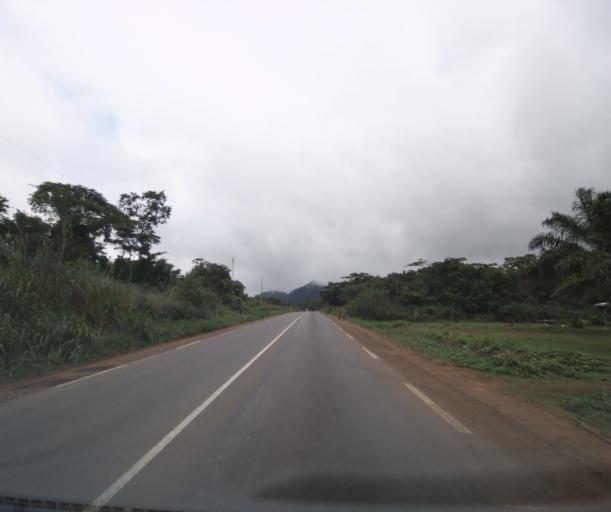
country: CM
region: Centre
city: Mbankomo
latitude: 3.8005
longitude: 11.3480
